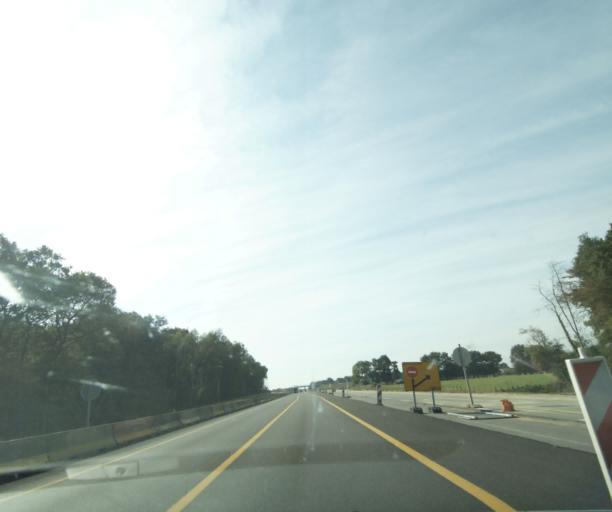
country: FR
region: Bourgogne
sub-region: Departement de Saone-et-Loire
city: Palinges
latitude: 46.5197
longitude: 4.1639
